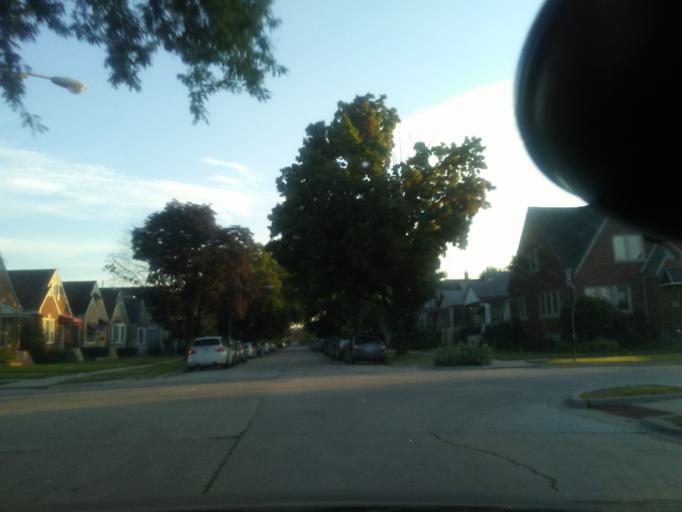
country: US
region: Illinois
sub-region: Cook County
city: Harwood Heights
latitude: 41.9773
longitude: -87.7796
